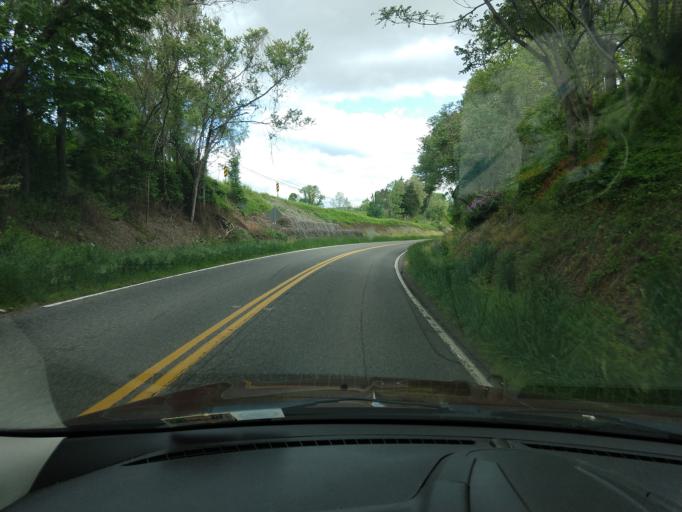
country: US
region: Virginia
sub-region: Wythe County
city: Wytheville
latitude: 36.8438
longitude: -80.9710
